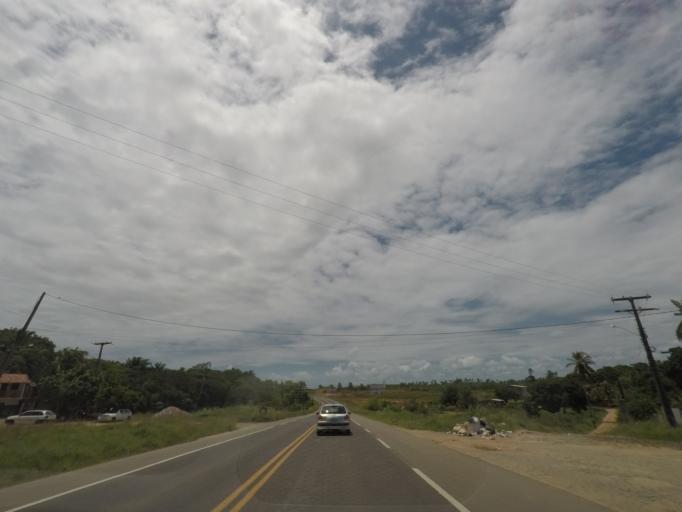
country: BR
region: Bahia
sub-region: Itaparica
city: Itaparica
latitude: -12.9400
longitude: -38.6293
